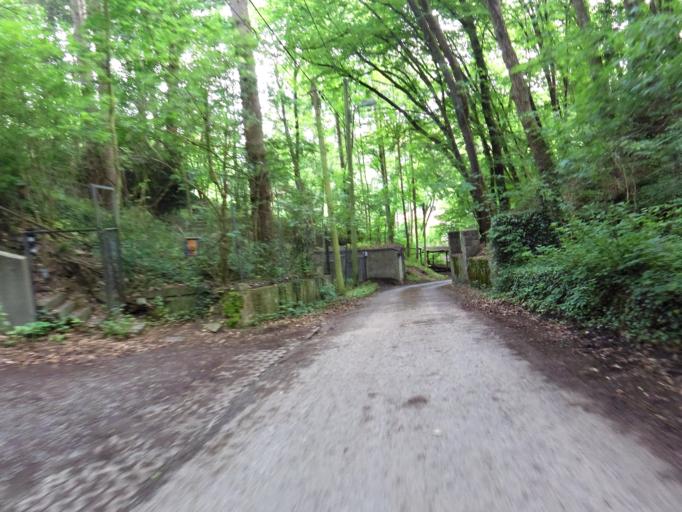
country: DE
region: Bavaria
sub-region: Regierungsbezirk Unterfranken
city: Wuerzburg
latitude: 49.7703
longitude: 9.8893
